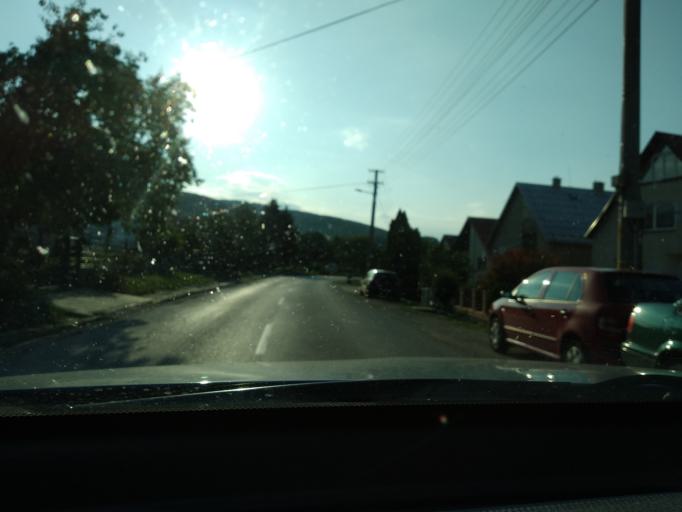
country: SK
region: Trenciansky
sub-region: Okres Trencin
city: Trencin
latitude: 48.8032
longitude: 18.1042
